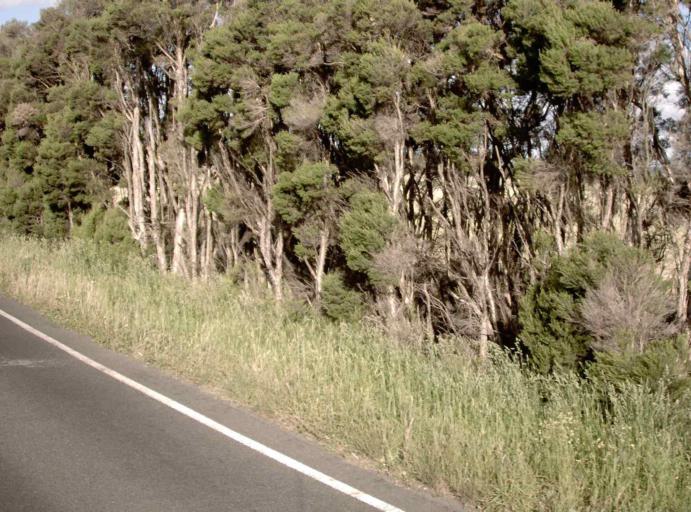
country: AU
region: Victoria
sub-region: Bass Coast
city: North Wonthaggi
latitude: -38.5070
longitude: 145.9102
